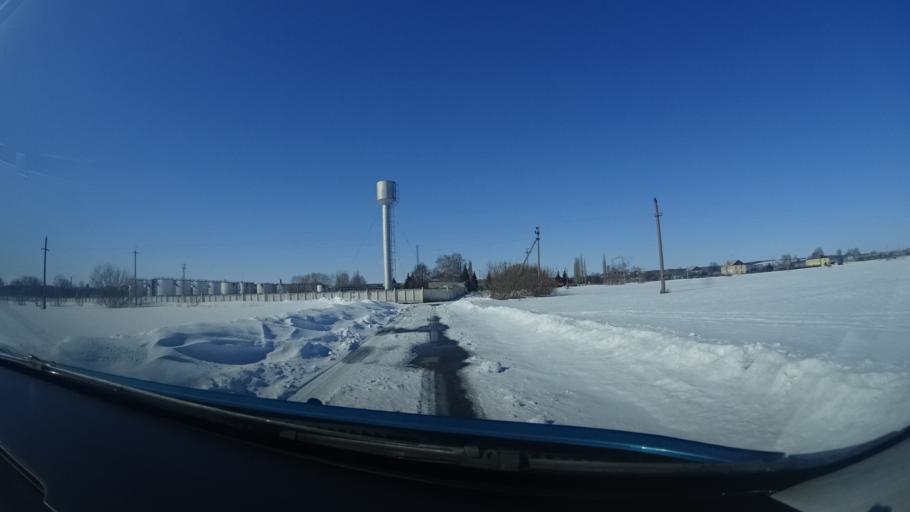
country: RU
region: Bashkortostan
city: Chishmy
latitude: 54.5869
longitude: 55.4098
